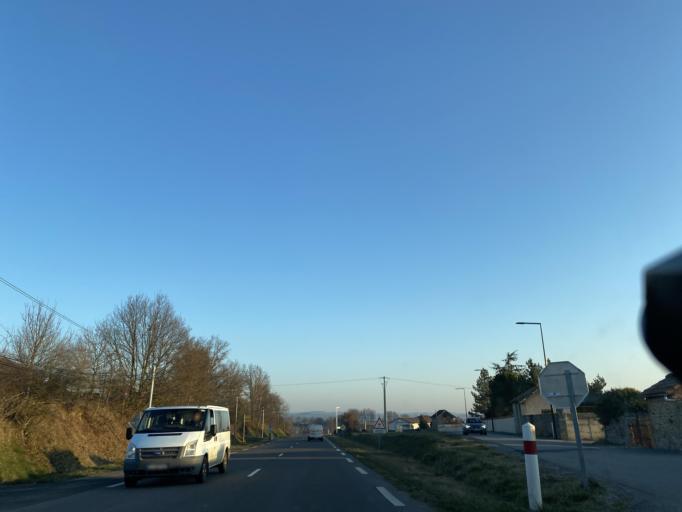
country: FR
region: Rhone-Alpes
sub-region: Departement de la Loire
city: Saint-Germain-Laval
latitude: 45.8363
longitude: 4.0150
